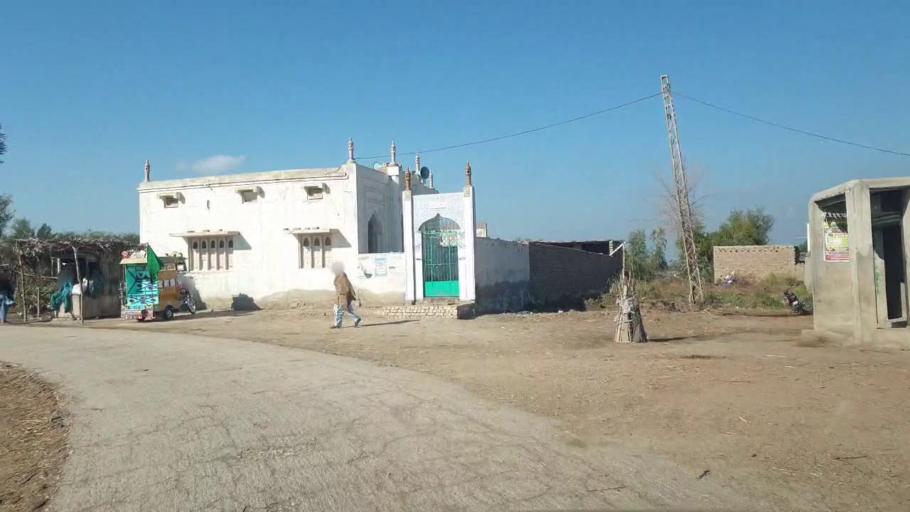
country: PK
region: Sindh
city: Shahdadpur
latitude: 25.9170
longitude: 68.5307
